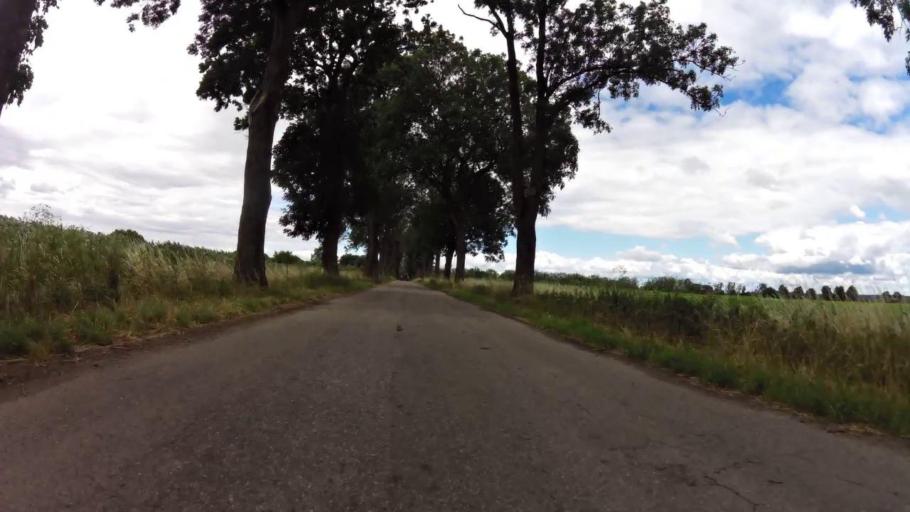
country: PL
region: West Pomeranian Voivodeship
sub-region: Powiat lobeski
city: Radowo Male
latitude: 53.7611
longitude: 15.5474
